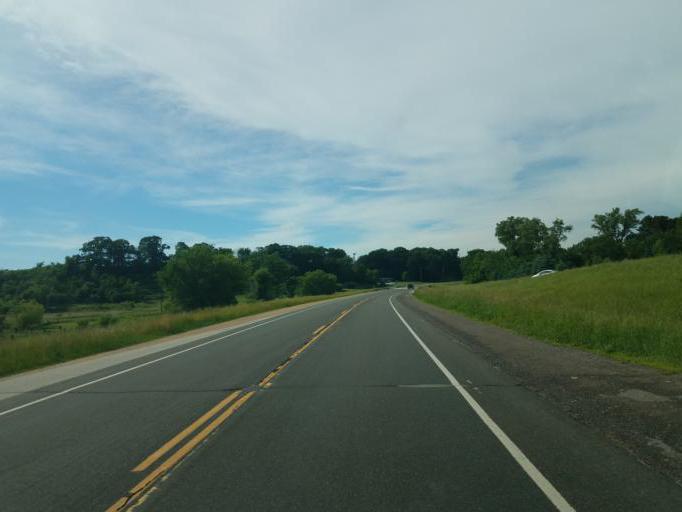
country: US
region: Wisconsin
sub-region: Monroe County
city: Tomah
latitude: 43.9267
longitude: -90.5016
